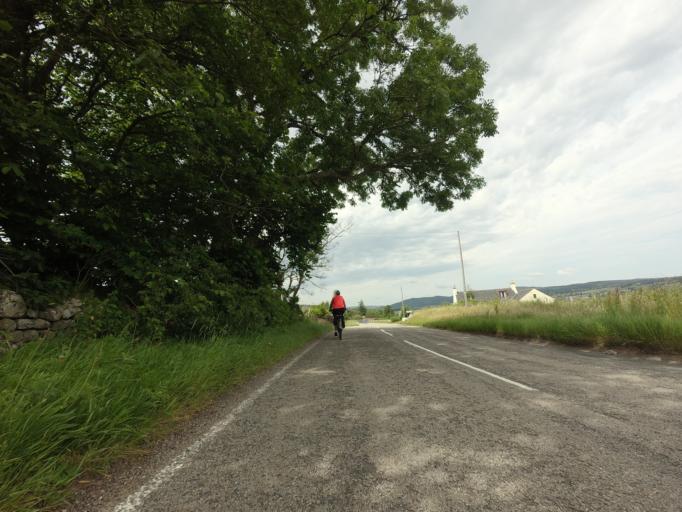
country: GB
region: Scotland
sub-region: Highland
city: Alness
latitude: 57.8728
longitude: -4.3530
